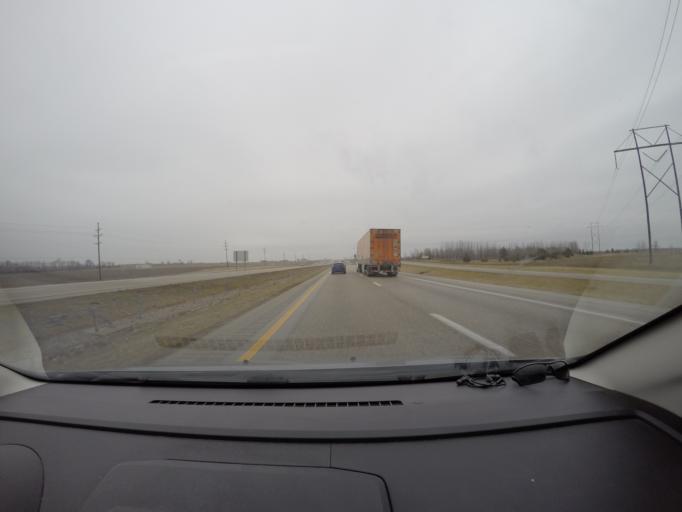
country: US
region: Missouri
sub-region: Montgomery County
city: Montgomery City
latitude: 38.8928
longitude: -91.4329
